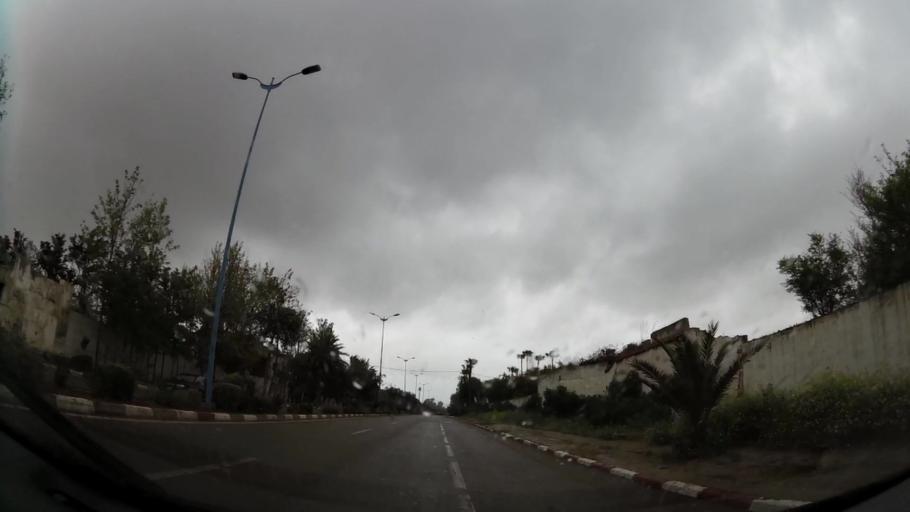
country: MA
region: Grand Casablanca
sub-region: Casablanca
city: Casablanca
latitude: 33.5257
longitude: -7.6312
